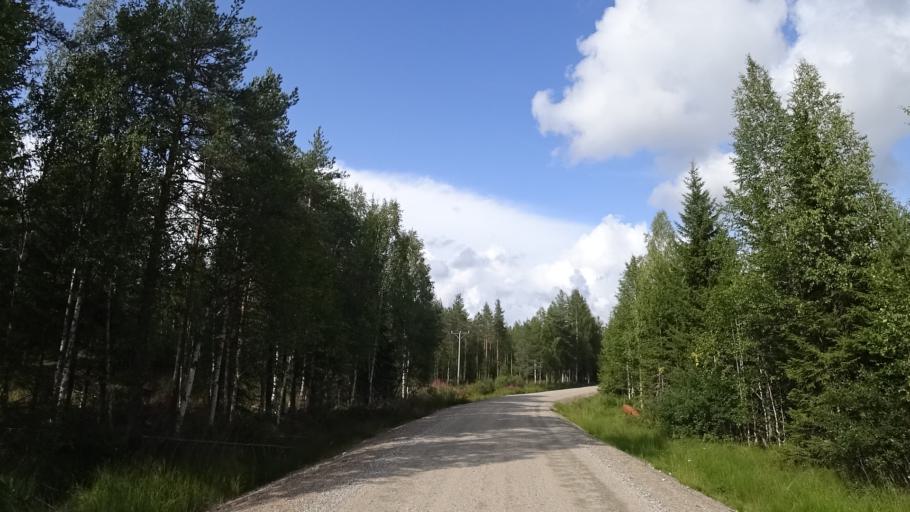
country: FI
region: North Karelia
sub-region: Pielisen Karjala
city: Lieksa
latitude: 63.5908
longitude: 30.1354
